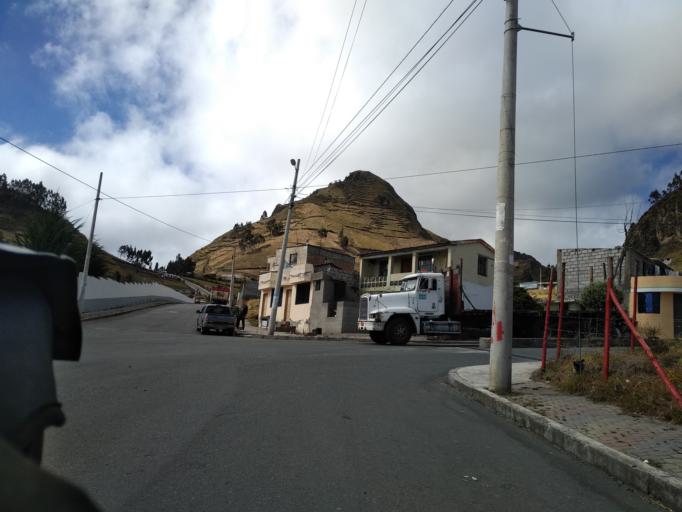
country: EC
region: Cotopaxi
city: Pujili
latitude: -0.9633
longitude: -78.8985
